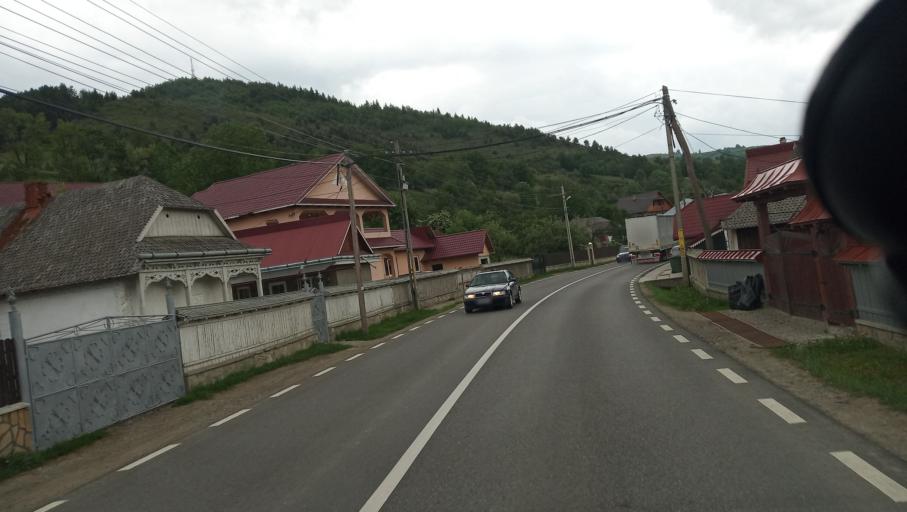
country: RO
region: Neamt
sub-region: Comuna Pipirig
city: Dolhesti
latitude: 47.2297
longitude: 26.0913
